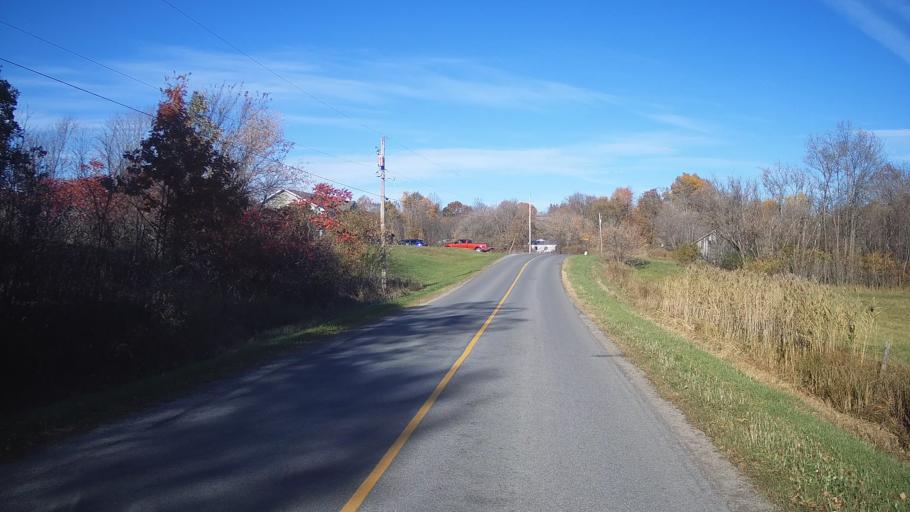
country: CA
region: Ontario
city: Kingston
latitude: 44.4425
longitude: -76.5219
